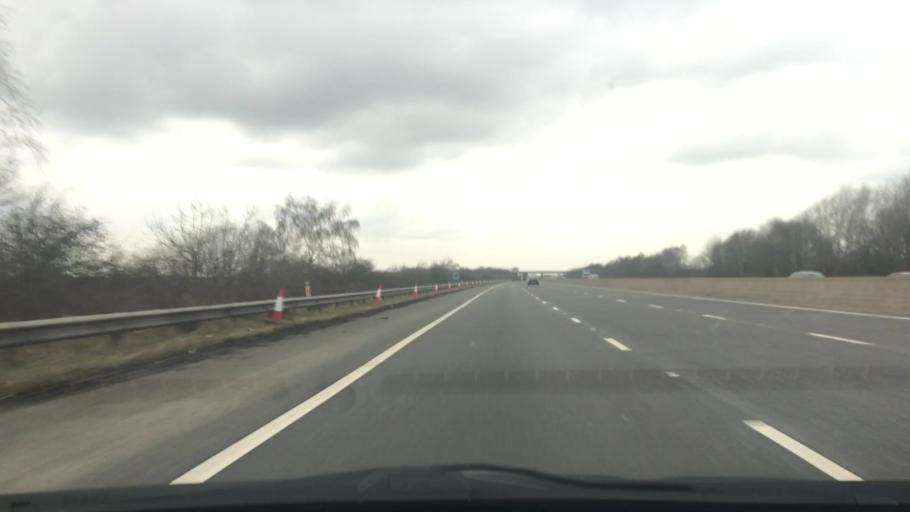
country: GB
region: England
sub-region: North Lincolnshire
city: Crowle
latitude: 53.5740
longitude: -0.9113
